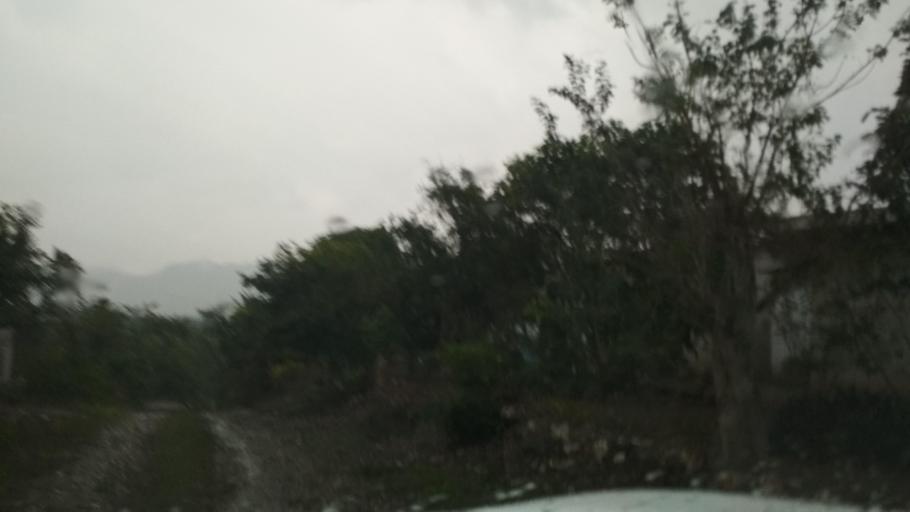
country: MM
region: Shan
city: Taunggyi
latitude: 20.3020
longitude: 97.3028
